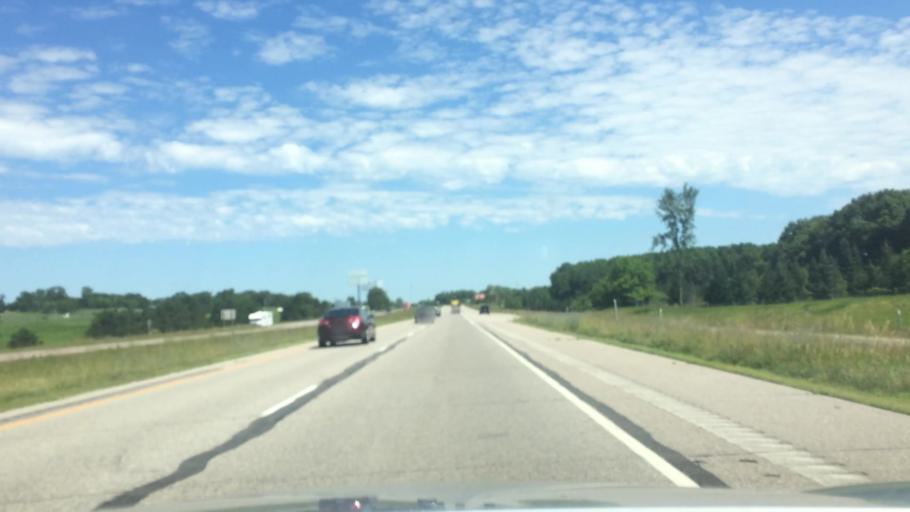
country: US
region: Wisconsin
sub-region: Columbia County
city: Portage
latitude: 43.7027
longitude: -89.4711
